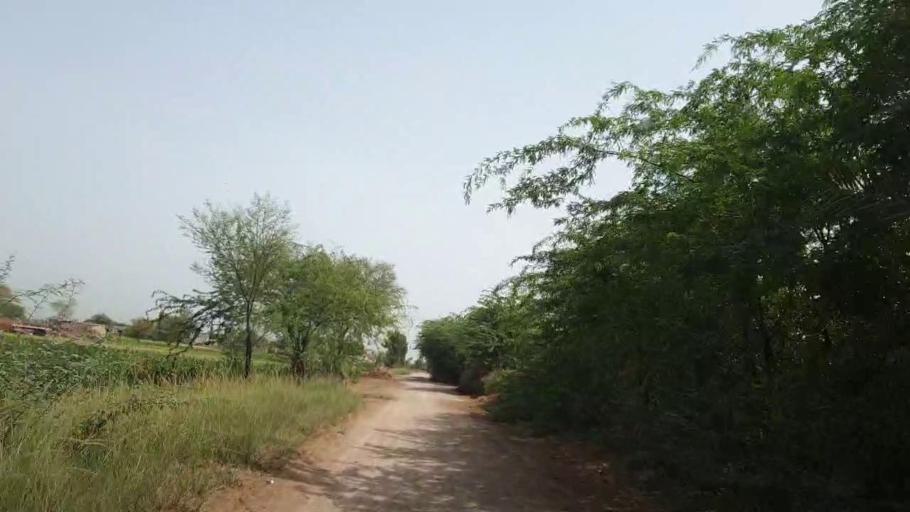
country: PK
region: Sindh
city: Sakrand
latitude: 26.1216
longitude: 68.3695
